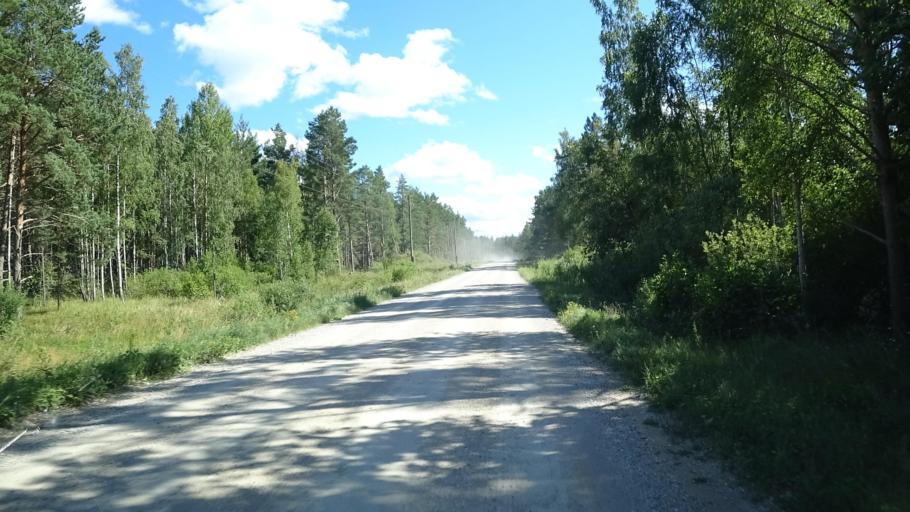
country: LV
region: Dundaga
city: Dundaga
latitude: 57.5918
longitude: 21.9847
